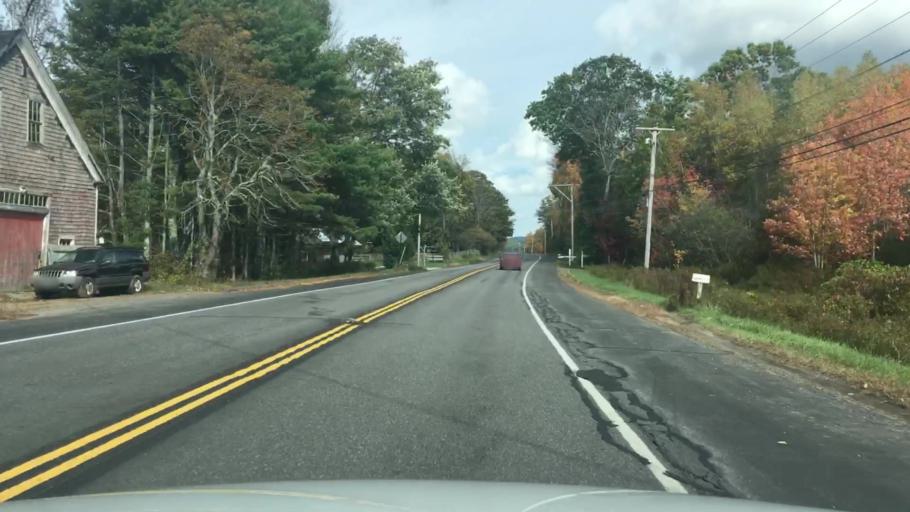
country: US
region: Maine
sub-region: Knox County
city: Rockport
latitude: 44.1616
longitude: -69.1179
